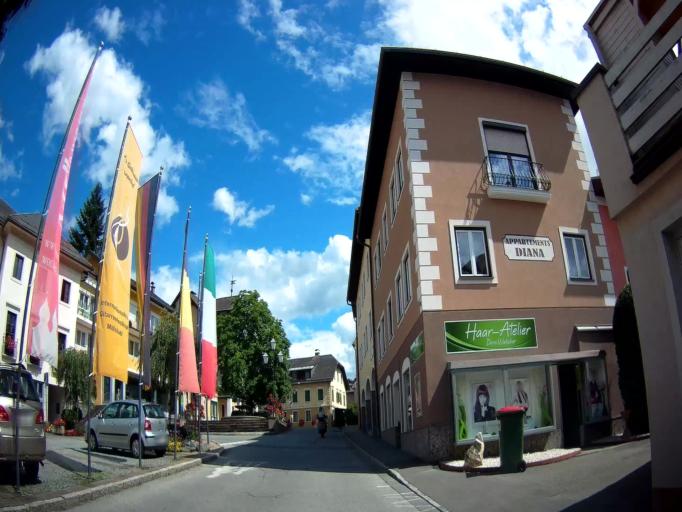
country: AT
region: Carinthia
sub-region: Politischer Bezirk Spittal an der Drau
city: Millstatt
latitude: 46.8050
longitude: 13.5714
